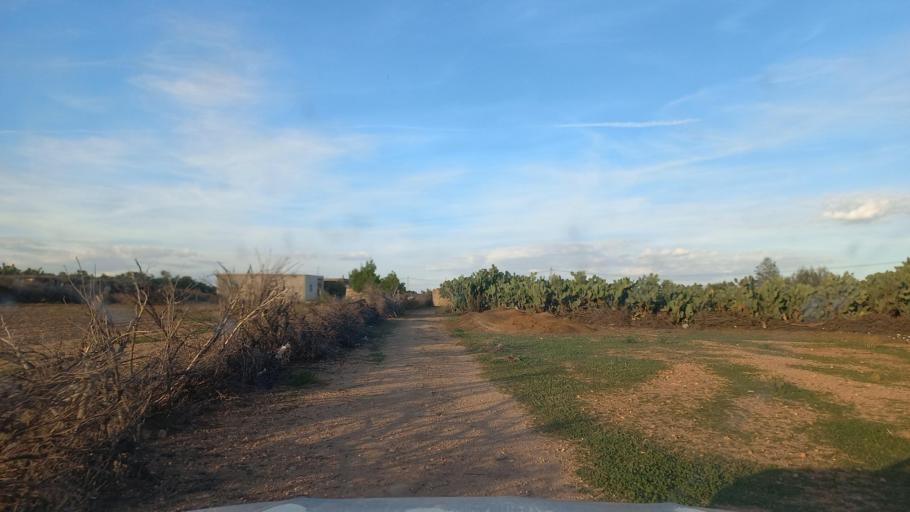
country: TN
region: Al Qasrayn
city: Sbiba
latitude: 35.3550
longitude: 9.0335
